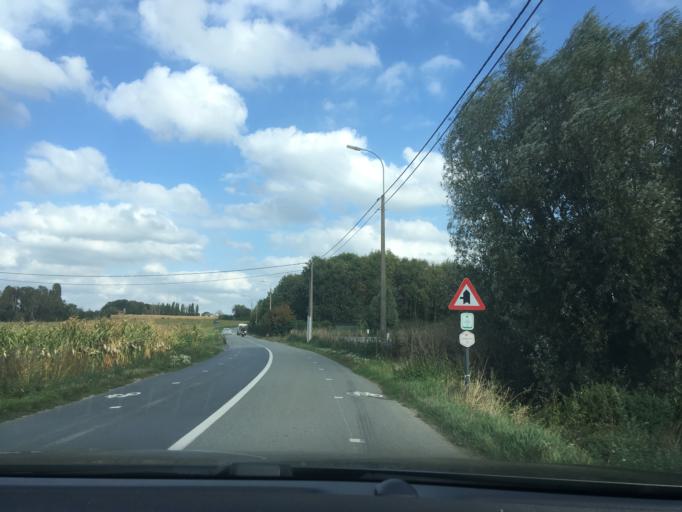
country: BE
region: Flanders
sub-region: Provincie West-Vlaanderen
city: Zonnebeke
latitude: 50.8949
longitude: 2.9902
